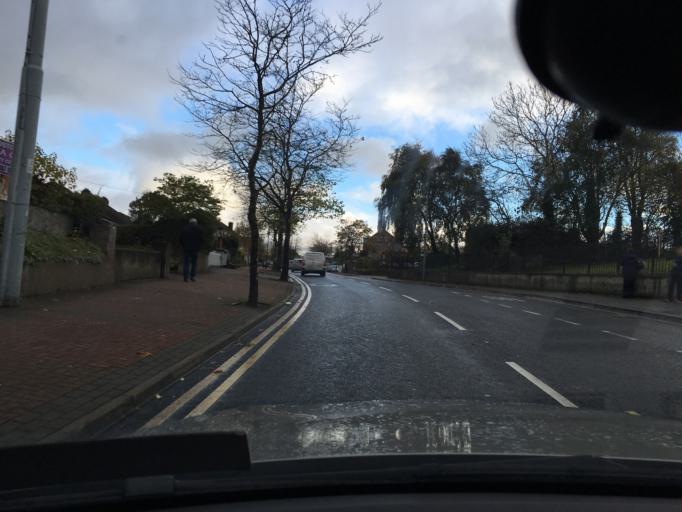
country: IE
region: Leinster
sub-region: Fingal County
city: Blanchardstown
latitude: 53.3877
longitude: -6.3791
